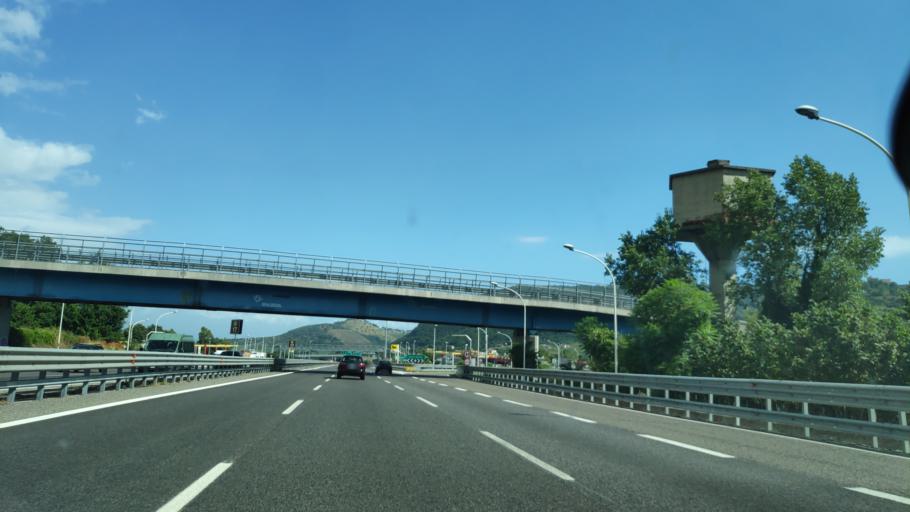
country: IT
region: Campania
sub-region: Provincia di Salerno
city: San Mango Piemonte
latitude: 40.6943
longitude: 14.8328
